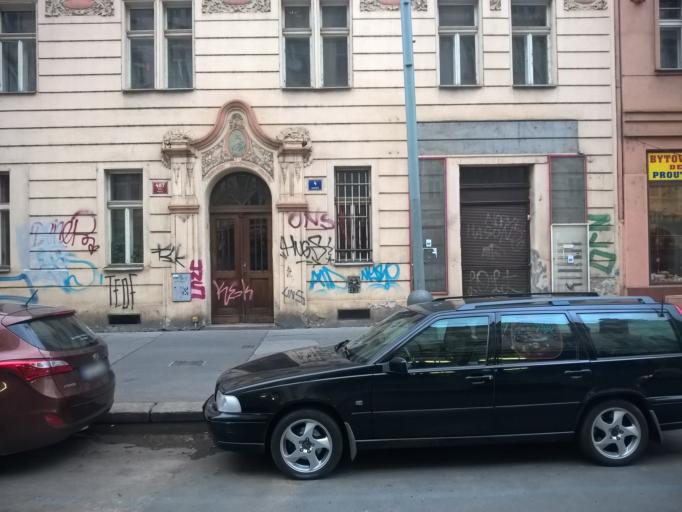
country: CZ
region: Praha
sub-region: Praha 2
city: Vysehrad
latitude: 50.0650
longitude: 14.4253
